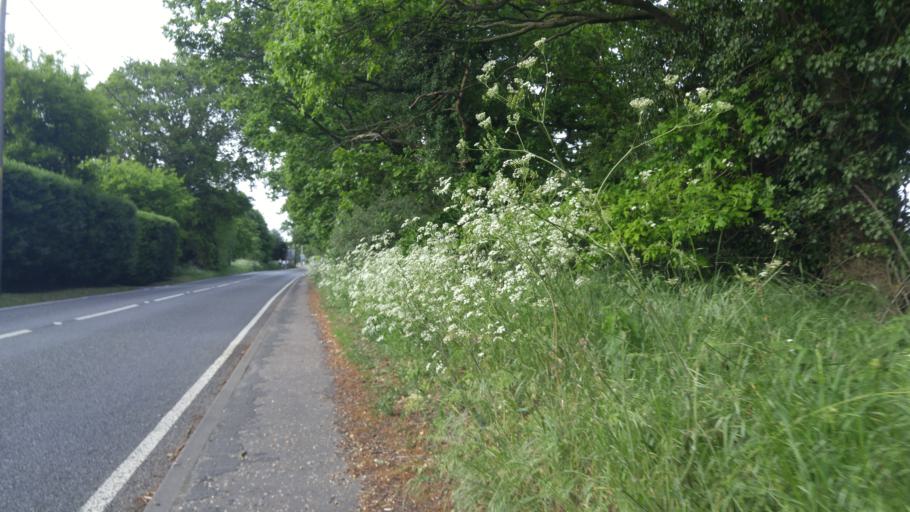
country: GB
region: England
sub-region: Essex
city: Layer de la Haye
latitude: 51.8625
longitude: 0.8696
